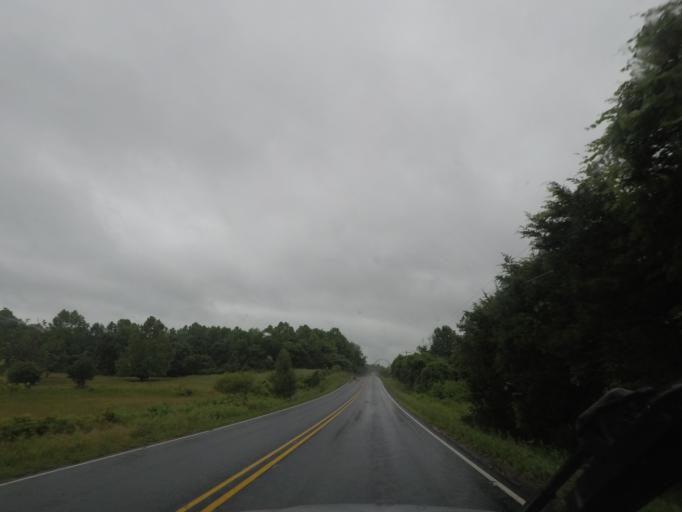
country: US
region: Virginia
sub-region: Culpeper County
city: Merrimac
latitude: 38.3714
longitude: -78.1006
